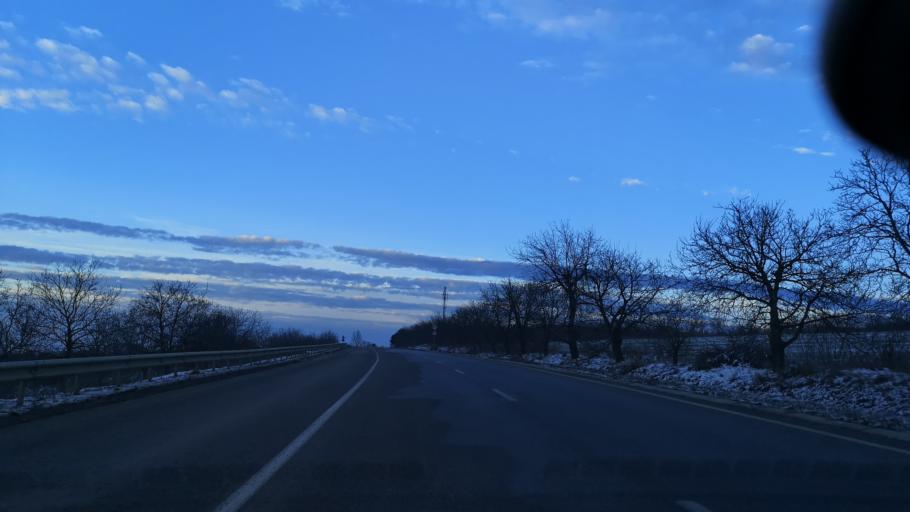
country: MD
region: Orhei
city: Orhei
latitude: 47.5316
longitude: 28.7947
